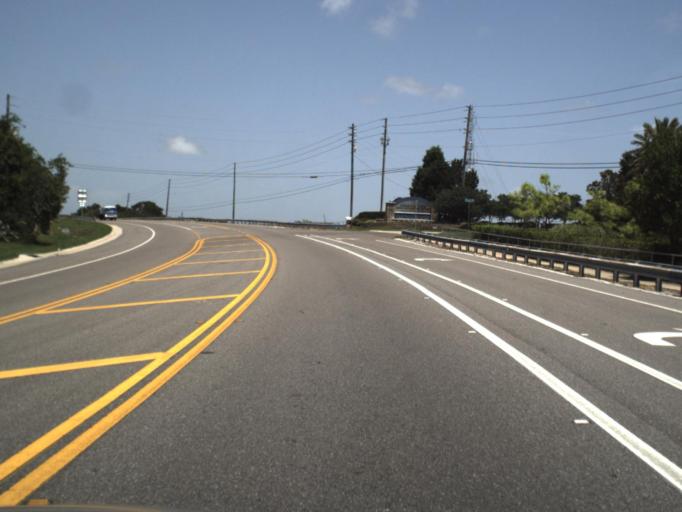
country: US
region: Florida
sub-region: Pinellas County
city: Palm Harbor
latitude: 28.1071
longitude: -82.7685
